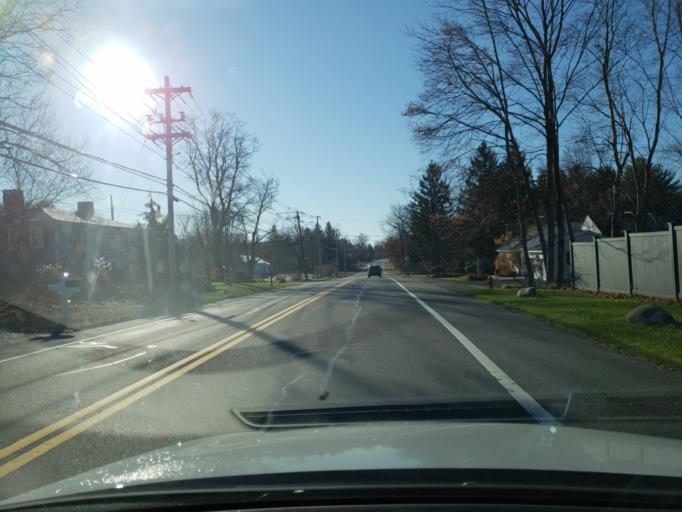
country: US
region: Massachusetts
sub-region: Essex County
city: Andover
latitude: 42.6284
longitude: -71.1271
